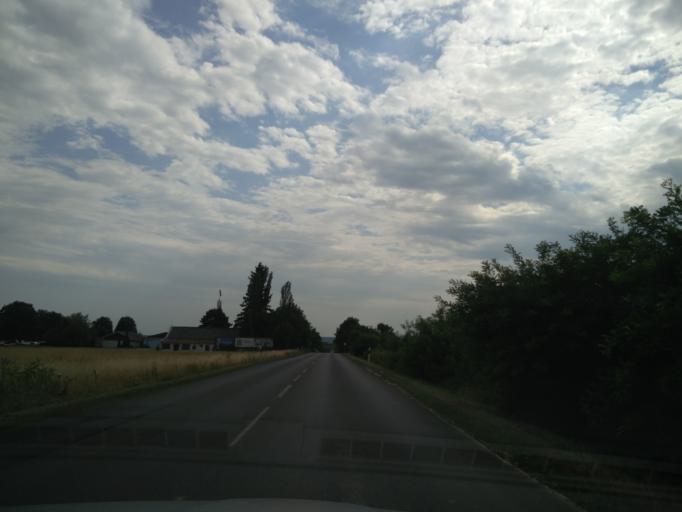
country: HU
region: Pest
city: Budakeszi
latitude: 47.4916
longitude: 18.9107
